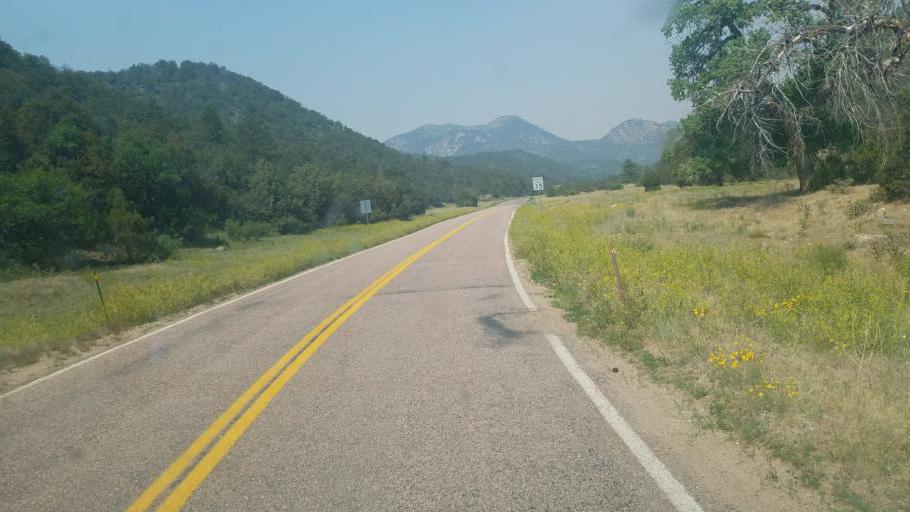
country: US
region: Colorado
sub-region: Fremont County
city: Canon City
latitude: 38.4128
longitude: -105.4160
